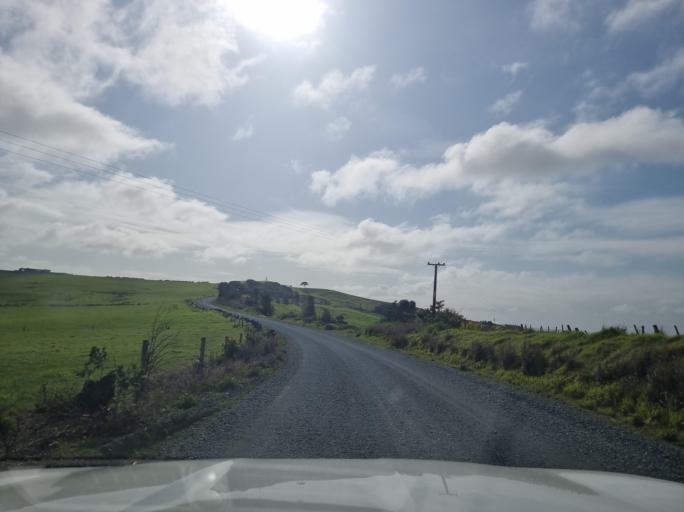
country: NZ
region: Northland
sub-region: Whangarei
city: Ruakaka
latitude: -36.0123
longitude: 174.4709
